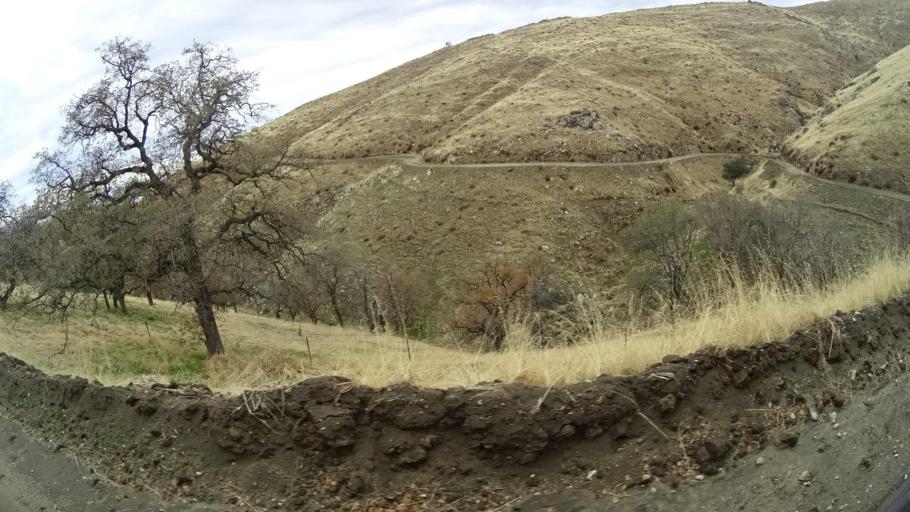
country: US
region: California
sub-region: Kern County
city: Arvin
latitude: 35.1260
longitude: -118.7539
